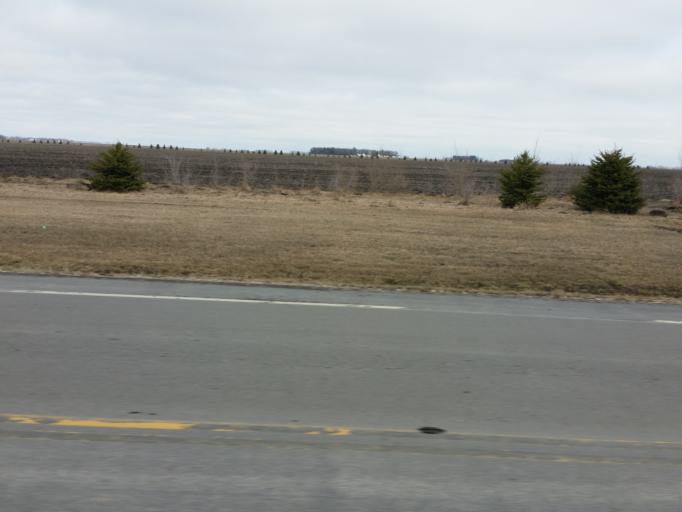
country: US
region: North Dakota
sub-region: Cass County
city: Casselton
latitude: 46.9053
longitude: -97.2173
